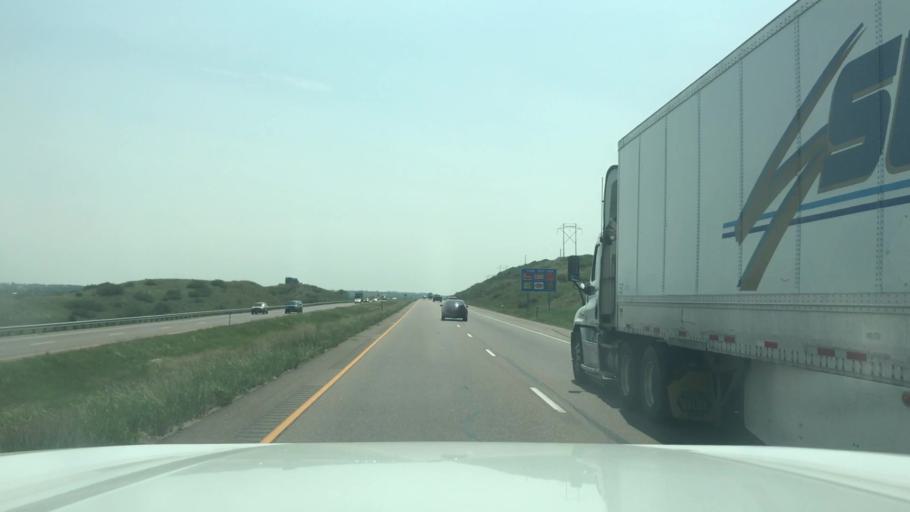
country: US
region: Colorado
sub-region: El Paso County
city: Security-Widefield
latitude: 38.7368
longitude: -104.7452
